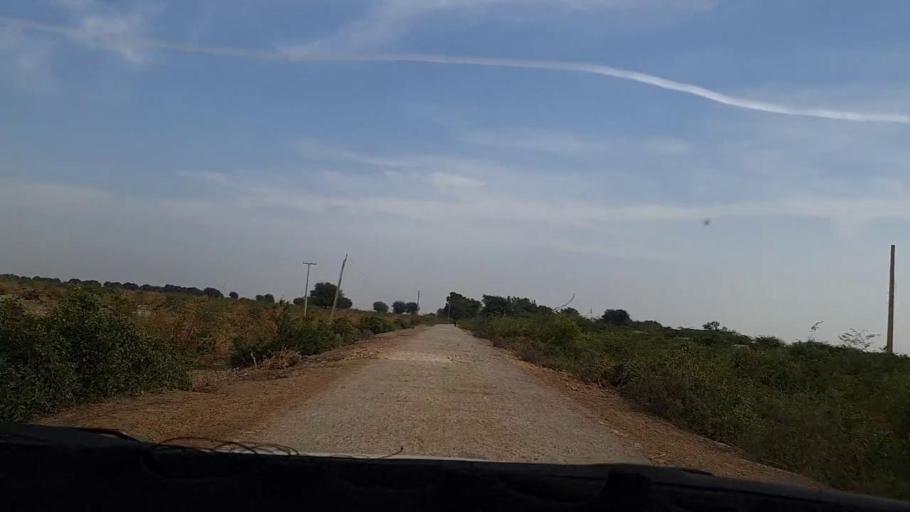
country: PK
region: Sindh
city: Pithoro
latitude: 25.5362
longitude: 69.3375
